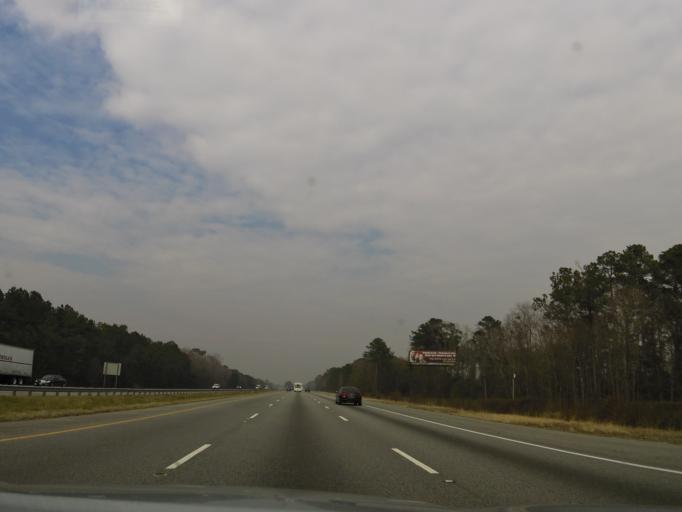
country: US
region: Georgia
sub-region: Liberty County
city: Midway
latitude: 31.6712
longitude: -81.3921
